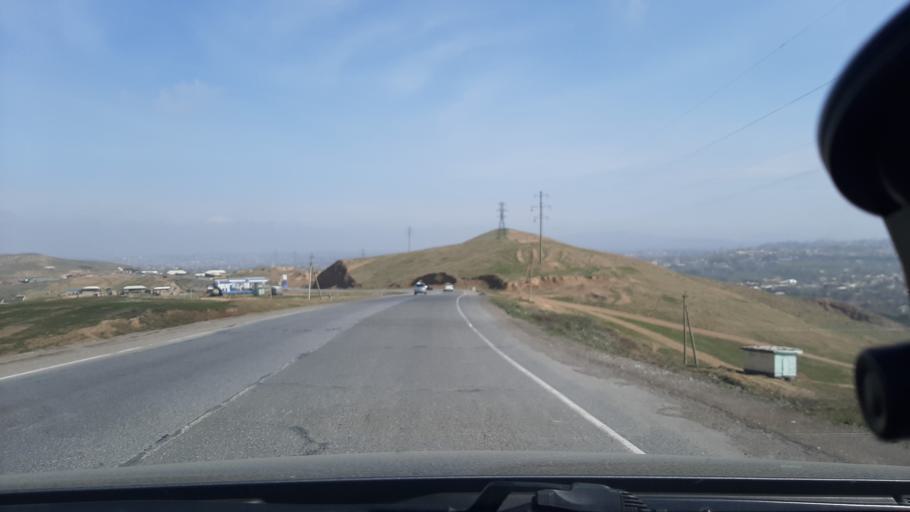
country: TJ
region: Viloyati Sughd
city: Istaravshan
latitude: 39.8517
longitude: 68.9849
